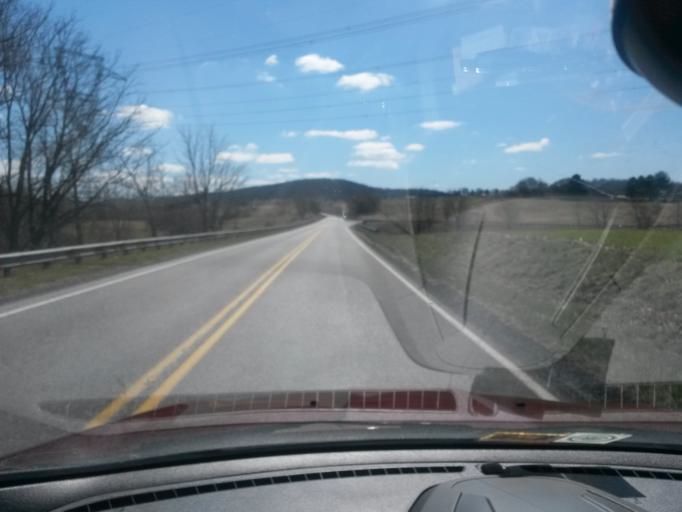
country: US
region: Virginia
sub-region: Augusta County
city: Jolivue
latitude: 38.0622
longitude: -79.0701
